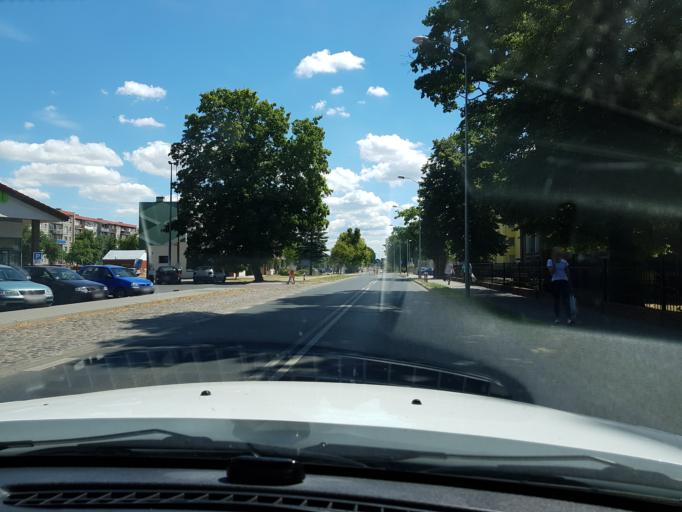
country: PL
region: West Pomeranian Voivodeship
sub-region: Powiat mysliborski
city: Mysliborz
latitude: 52.9248
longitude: 14.8736
